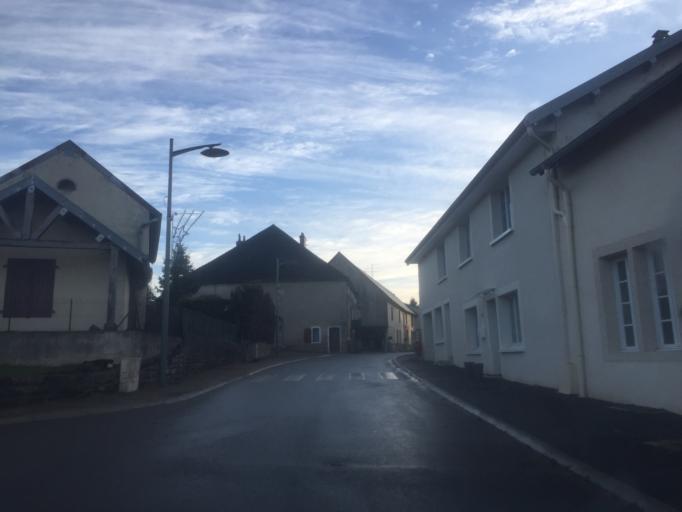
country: FR
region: Franche-Comte
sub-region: Departement du Jura
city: Dampierre
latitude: 47.1420
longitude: 5.7274
